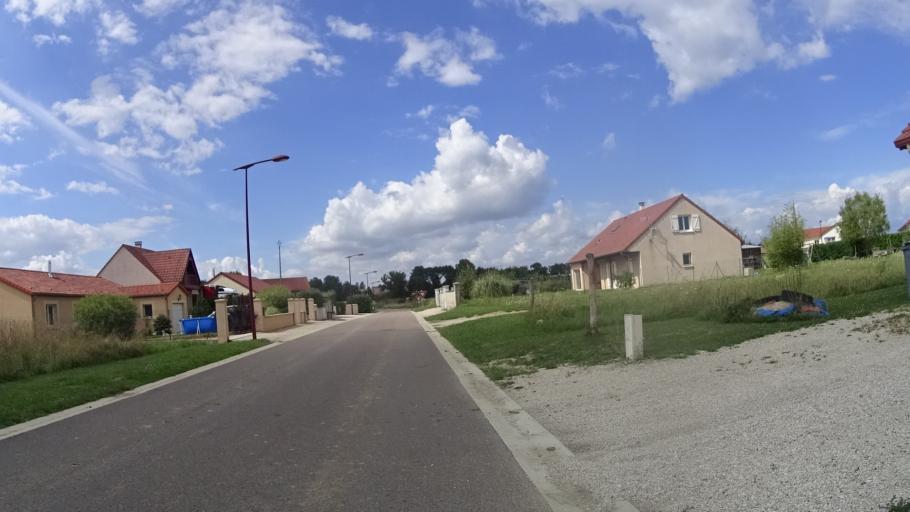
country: FR
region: Champagne-Ardenne
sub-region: Departement de la Marne
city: Pargny-sur-Saulx
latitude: 48.6905
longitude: 4.8053
